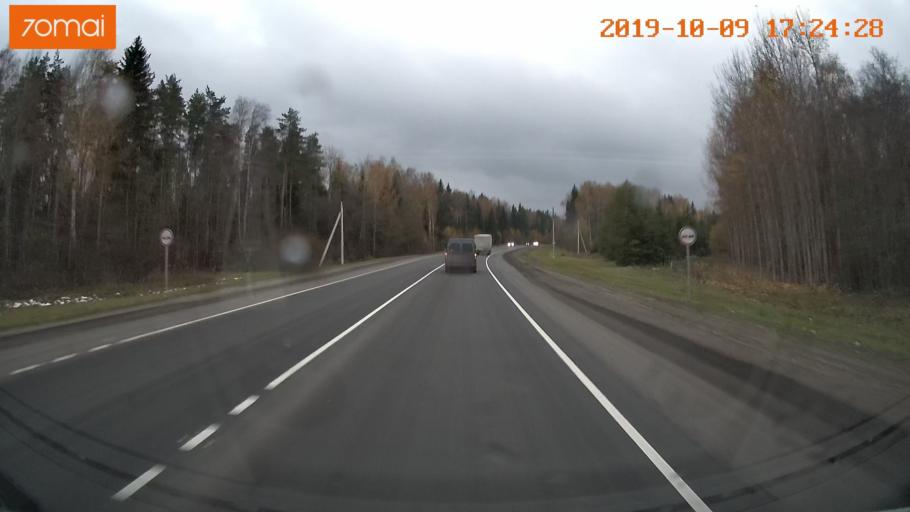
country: RU
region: Ivanovo
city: Furmanov
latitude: 57.1851
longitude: 41.1067
